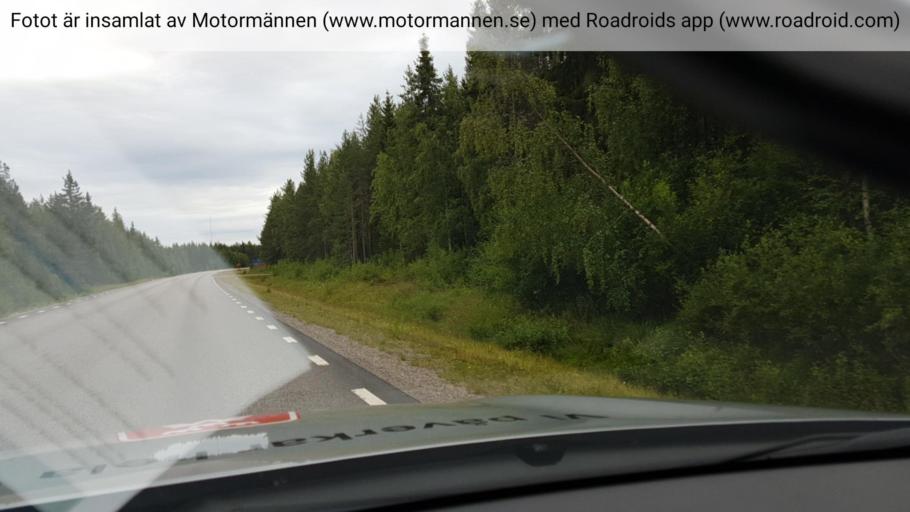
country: SE
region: Norrbotten
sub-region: Overkalix Kommun
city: OEverkalix
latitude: 66.3473
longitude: 22.8283
